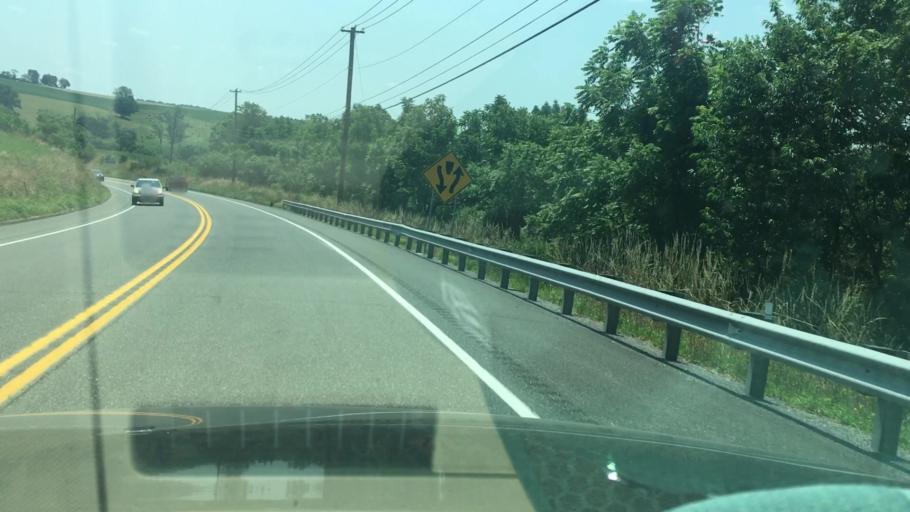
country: US
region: Pennsylvania
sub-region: Lehigh County
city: Schnecksville
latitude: 40.6378
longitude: -75.6814
